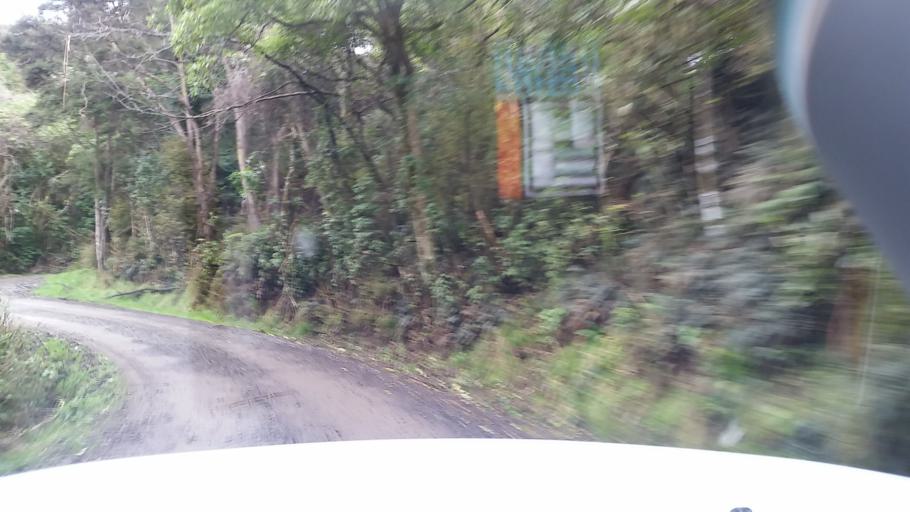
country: NZ
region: Canterbury
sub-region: Christchurch City
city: Christchurch
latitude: -43.6817
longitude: 172.7942
